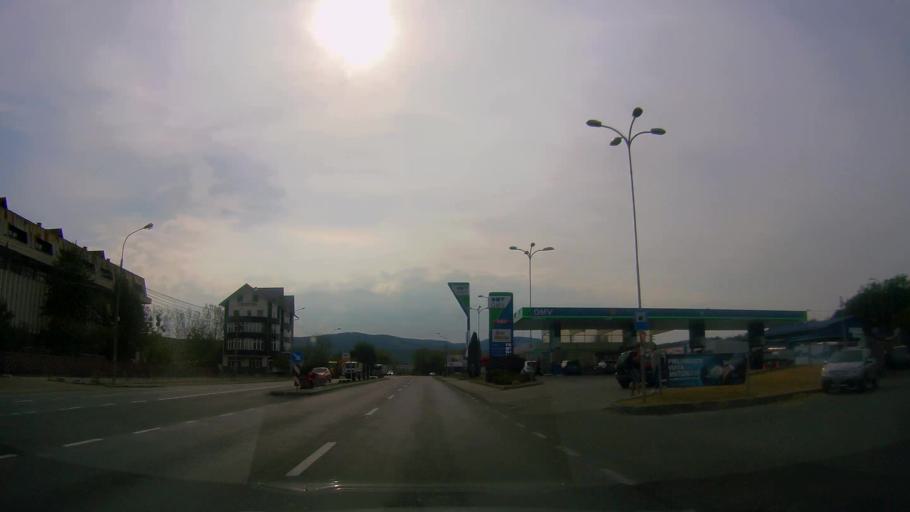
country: RO
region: Salaj
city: Zalau
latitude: 47.1986
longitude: 23.0580
